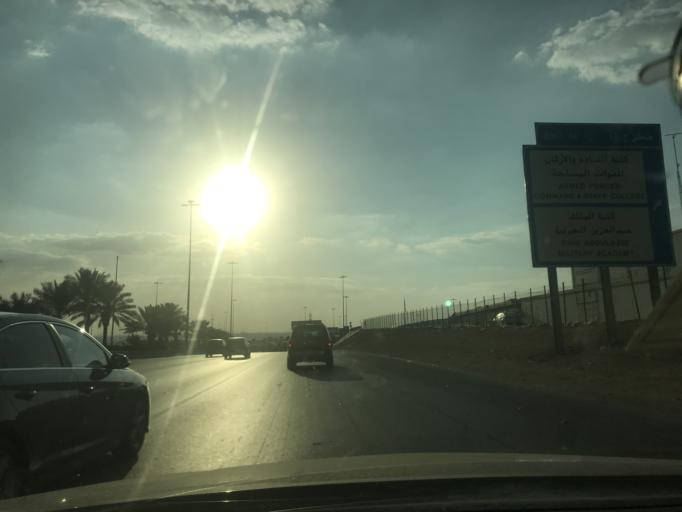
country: SA
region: Ar Riyad
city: Riyadh
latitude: 24.7395
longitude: 46.5956
